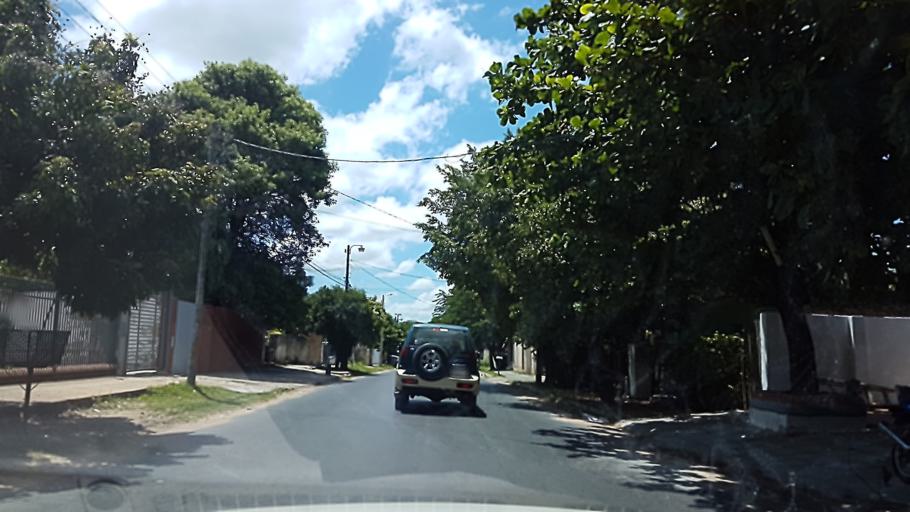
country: PY
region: Central
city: Colonia Mariano Roque Alonso
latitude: -25.2431
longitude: -57.5423
